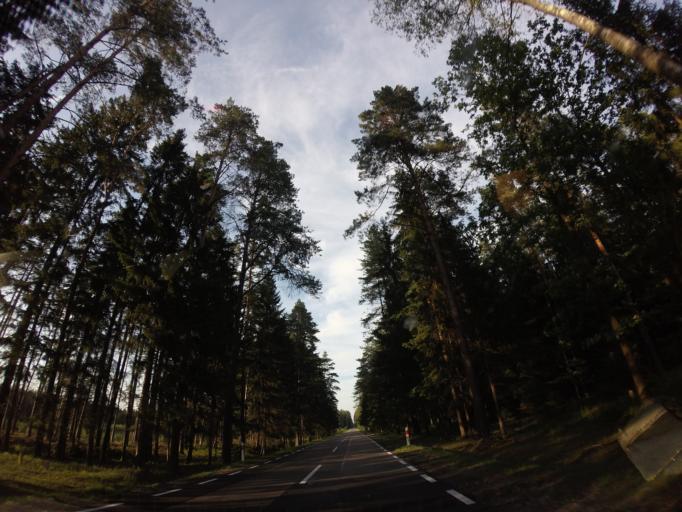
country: PL
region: Podlasie
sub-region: Powiat sejnenski
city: Krasnopol
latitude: 53.9261
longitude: 23.1578
